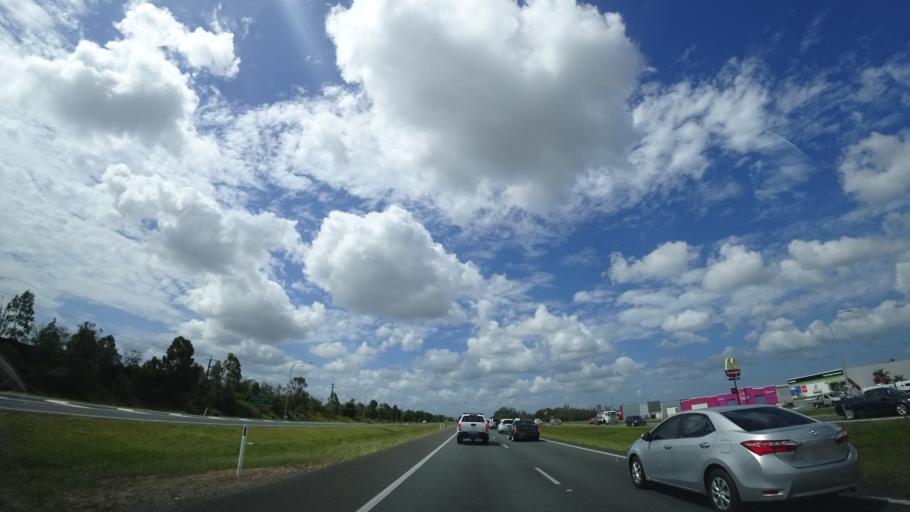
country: AU
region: Queensland
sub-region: Moreton Bay
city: Caboolture
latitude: -27.0811
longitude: 152.9756
